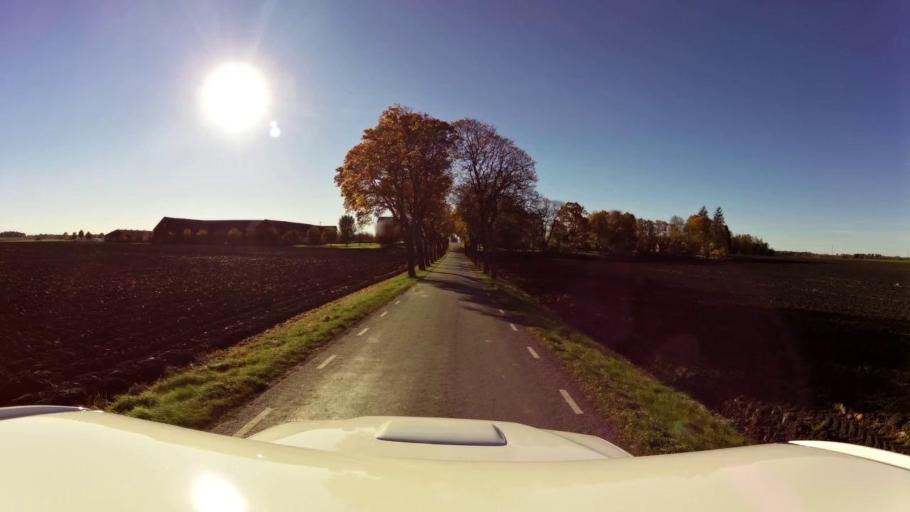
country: SE
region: OEstergoetland
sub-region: Linkopings Kommun
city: Ljungsbro
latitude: 58.5117
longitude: 15.4175
